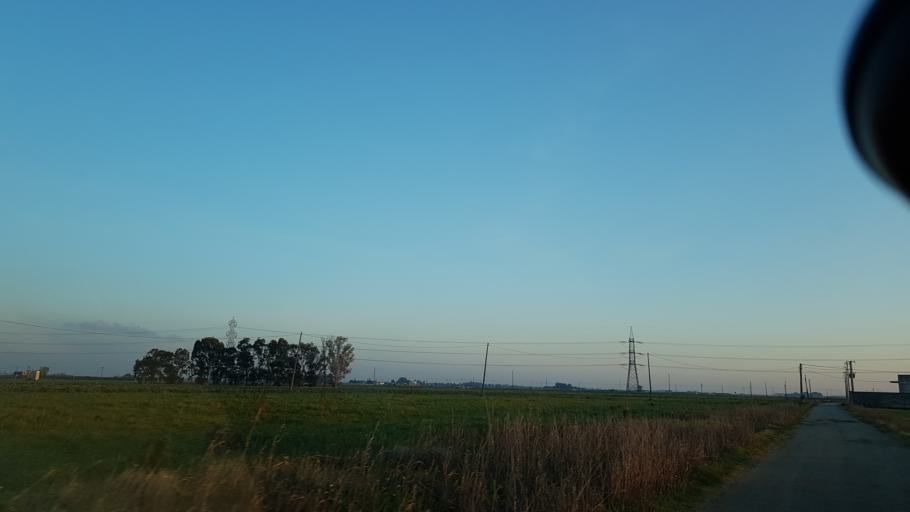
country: IT
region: Apulia
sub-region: Provincia di Brindisi
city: La Rosa
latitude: 40.5973
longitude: 17.9513
